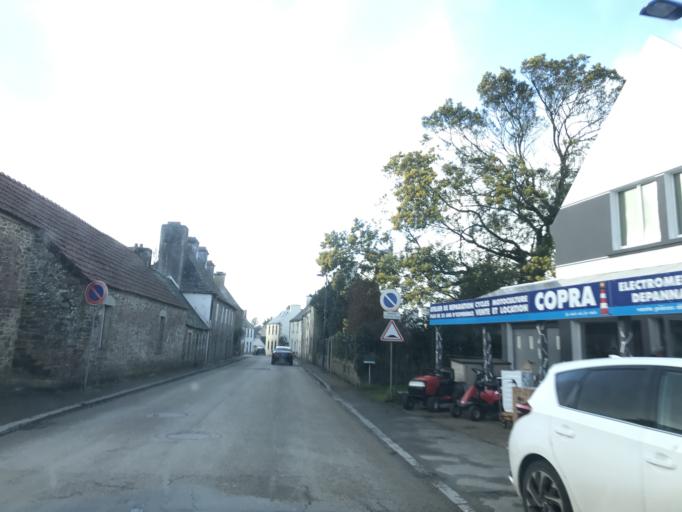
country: FR
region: Brittany
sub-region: Departement du Finistere
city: Lanmeur
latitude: 48.6463
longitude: -3.7134
